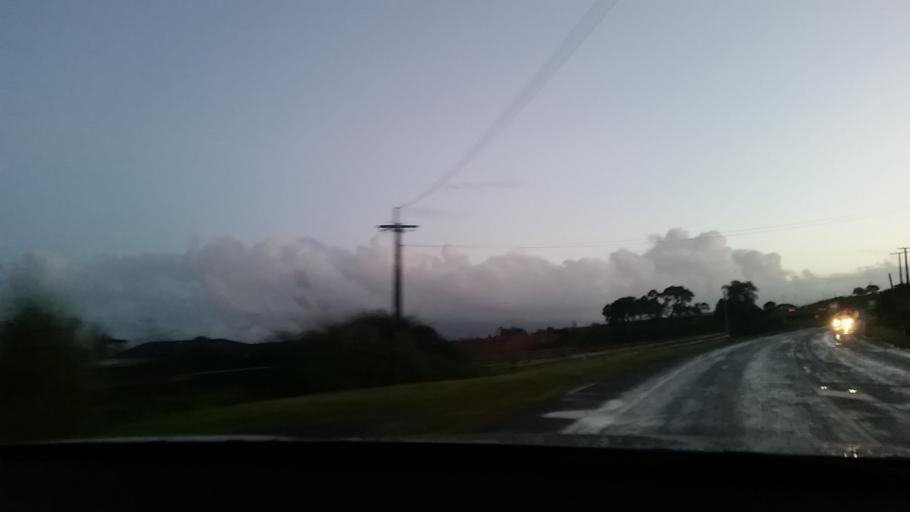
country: NZ
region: Waikato
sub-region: Hamilton City
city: Hamilton
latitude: -37.8154
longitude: 175.2306
